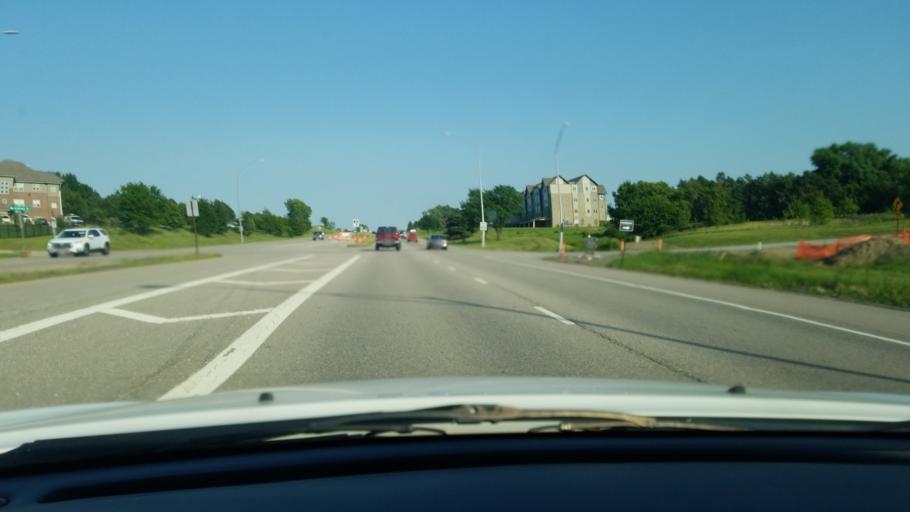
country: US
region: Nebraska
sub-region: Lancaster County
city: Lincoln
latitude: 40.7424
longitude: -96.6186
